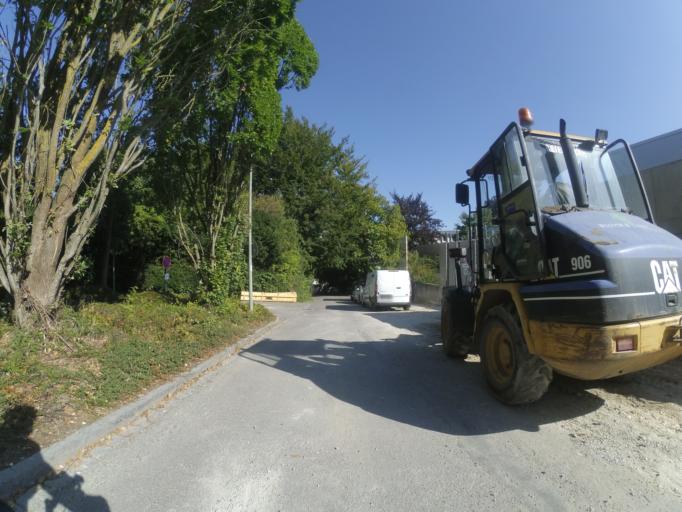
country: DE
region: Baden-Wuerttemberg
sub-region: Tuebingen Region
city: Ulm
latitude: 48.3860
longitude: 9.9561
